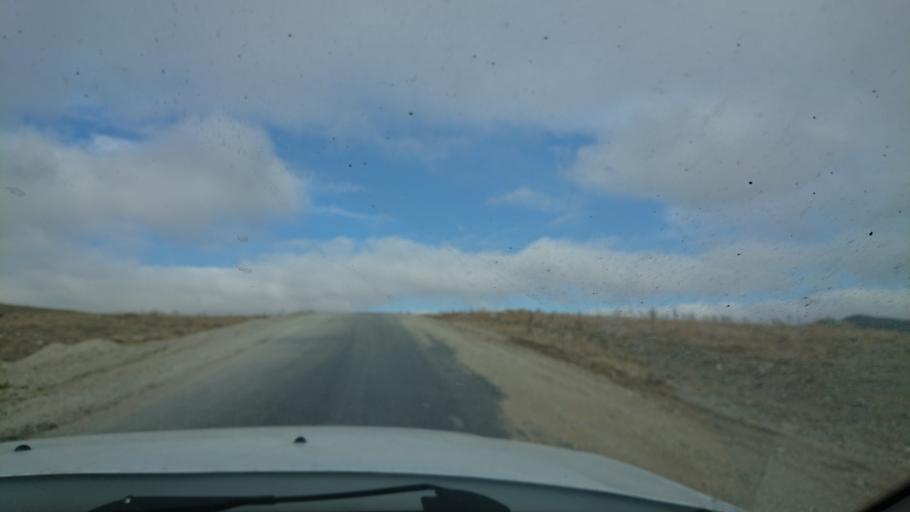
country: TR
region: Aksaray
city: Ortakoy
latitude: 38.7773
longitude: 34.0102
